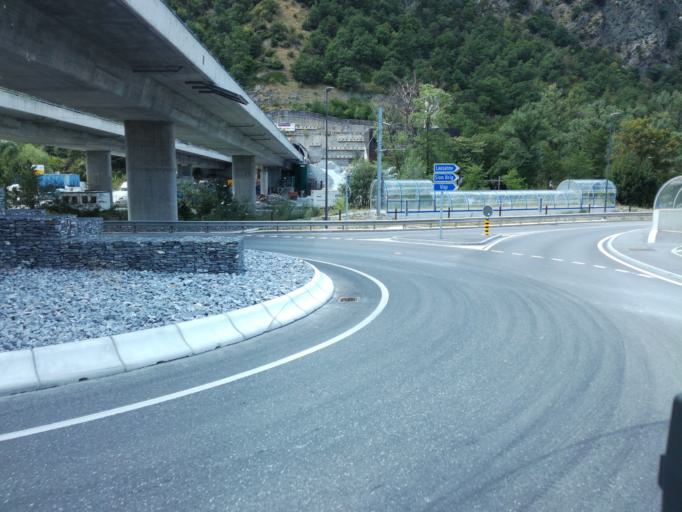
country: CH
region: Valais
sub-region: Visp District
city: Visp
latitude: 46.2920
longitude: 7.9146
